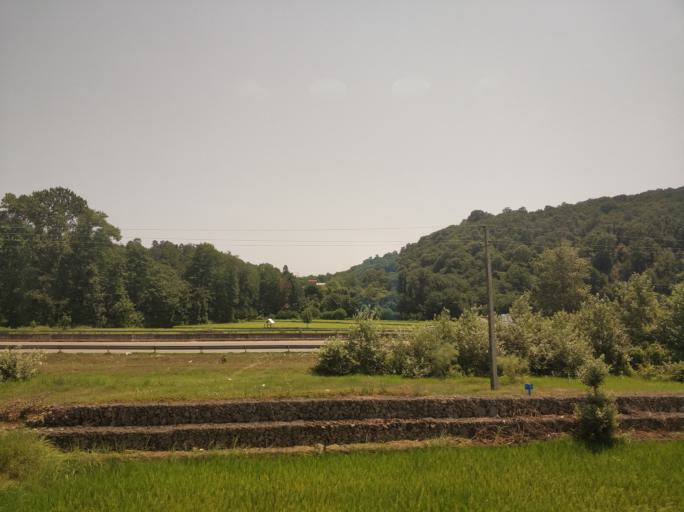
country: IR
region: Gilan
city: Pa'in-e Bazar-e Rudbar
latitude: 36.9607
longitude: 49.5536
